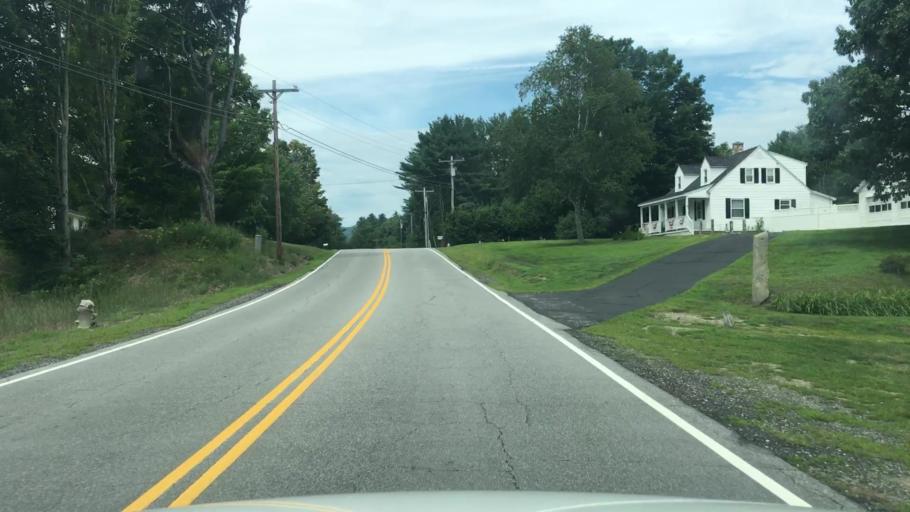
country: US
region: New Hampshire
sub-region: Grafton County
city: Rumney
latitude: 43.7858
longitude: -71.7715
